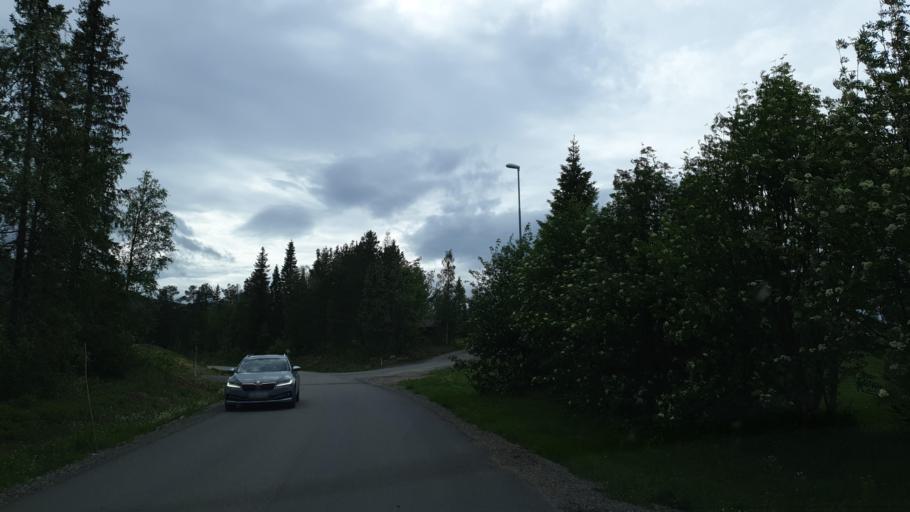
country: SE
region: Norrbotten
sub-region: Gallivare Kommun
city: Gaellivare
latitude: 67.1320
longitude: 20.6299
